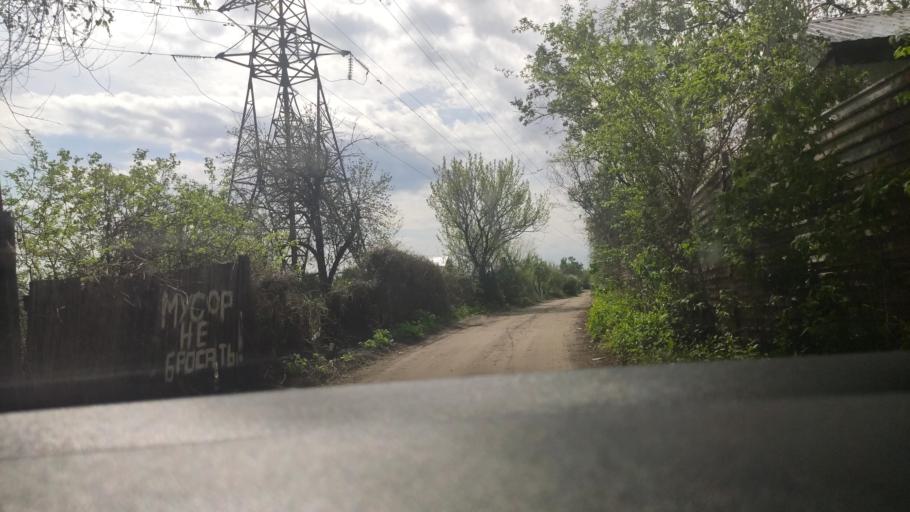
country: RU
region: Voronezj
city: Maslovka
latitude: 51.6065
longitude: 39.2863
